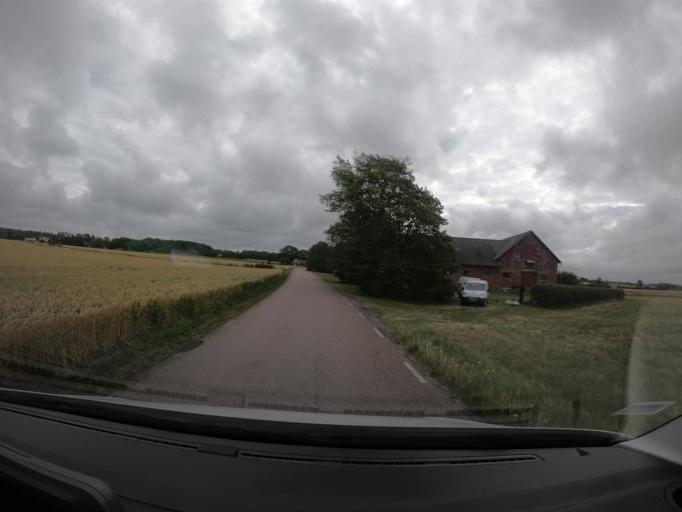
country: SE
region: Skane
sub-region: Angelholms Kommun
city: Vejbystrand
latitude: 56.3560
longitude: 12.7629
